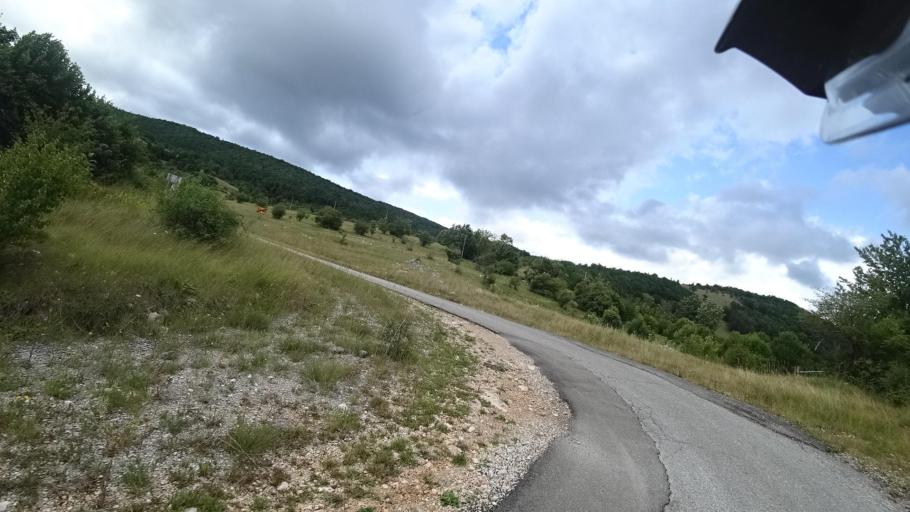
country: HR
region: Licko-Senjska
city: Jezerce
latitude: 44.7267
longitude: 15.5048
